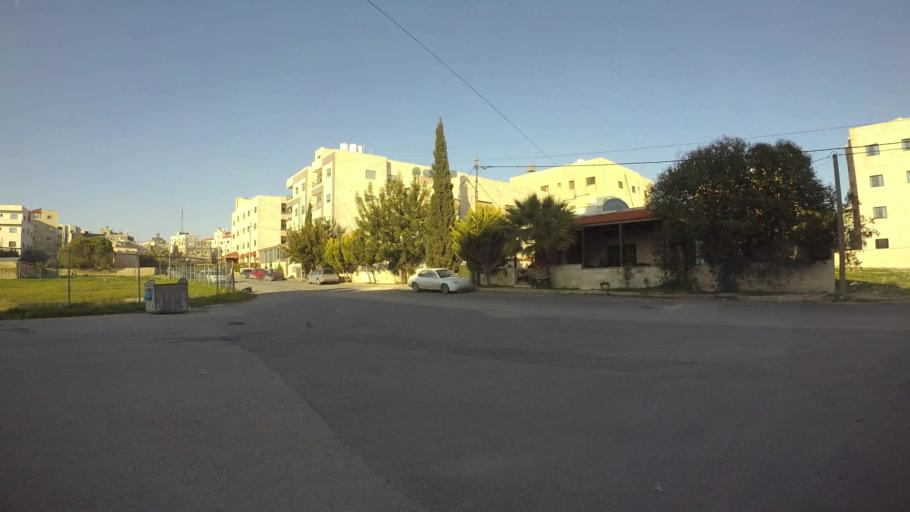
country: JO
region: Amman
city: Al Bunayyat ash Shamaliyah
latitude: 31.9000
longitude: 35.9063
